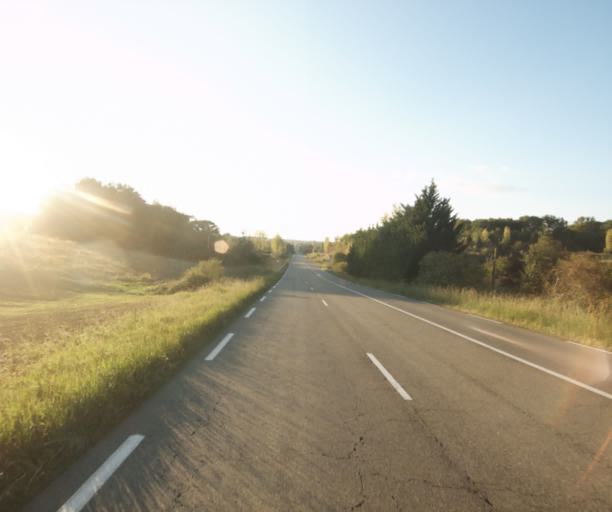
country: FR
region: Midi-Pyrenees
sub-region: Departement du Gers
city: Eauze
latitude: 43.7603
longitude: 0.1843
